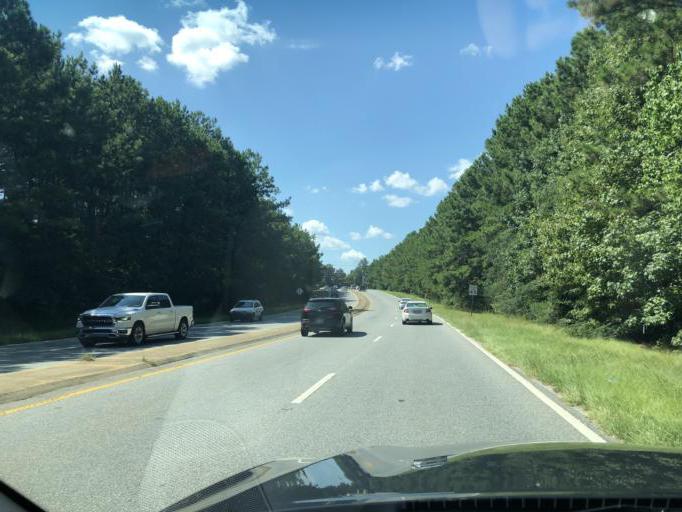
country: US
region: Georgia
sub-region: Muscogee County
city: Columbus
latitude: 32.5262
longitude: -84.9228
